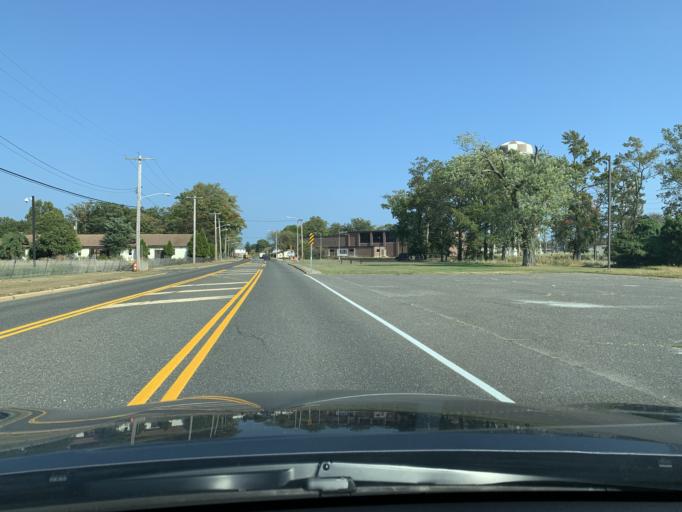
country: US
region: New Jersey
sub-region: Monmouth County
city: Eatontown
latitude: 40.3128
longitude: -74.0458
